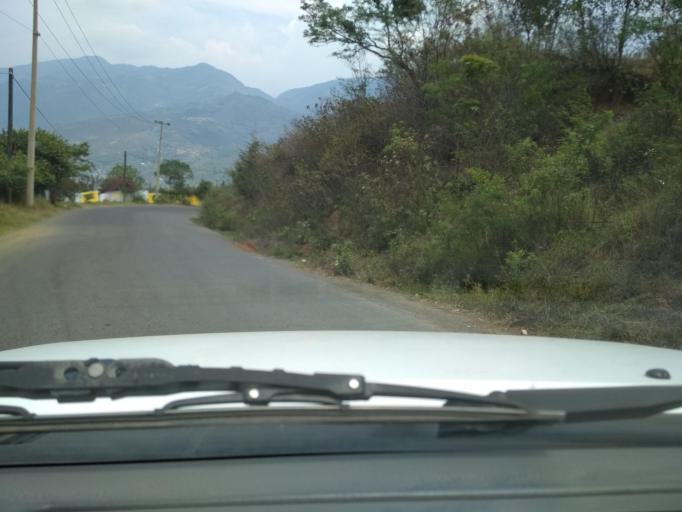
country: MX
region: Veracruz
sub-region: Camerino Z. Mendoza
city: La Cuesta
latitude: 18.7958
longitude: -97.1725
